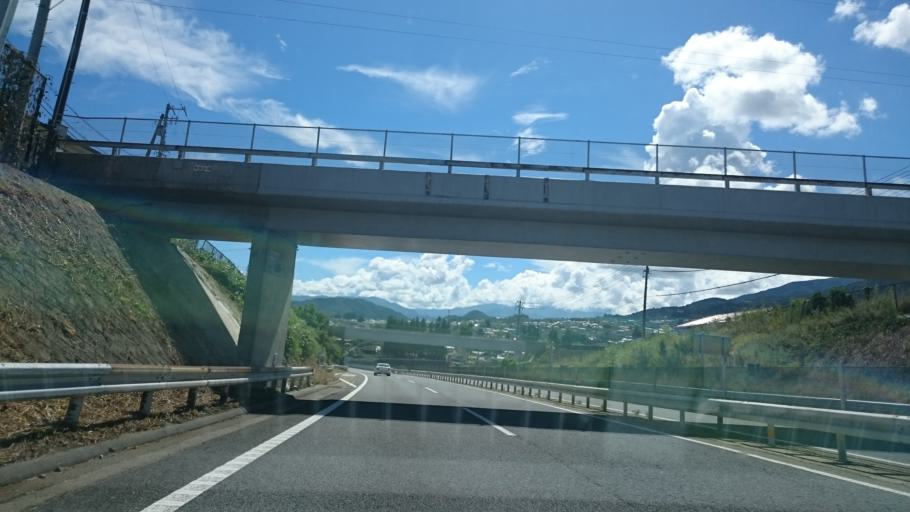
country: JP
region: Nagano
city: Iida
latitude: 35.5179
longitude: 137.8045
